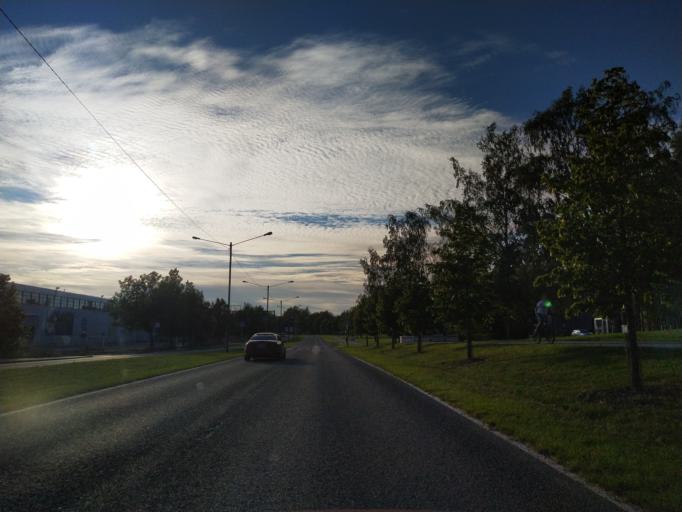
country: FI
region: Varsinais-Suomi
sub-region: Turku
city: Turku
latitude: 60.4473
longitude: 22.3231
